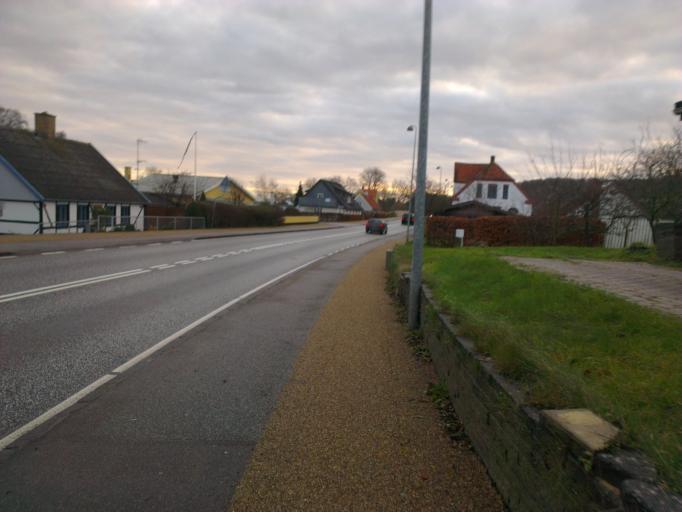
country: DK
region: Capital Region
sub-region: Frederikssund Kommune
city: Jaegerspris
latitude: 55.8554
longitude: 12.0003
